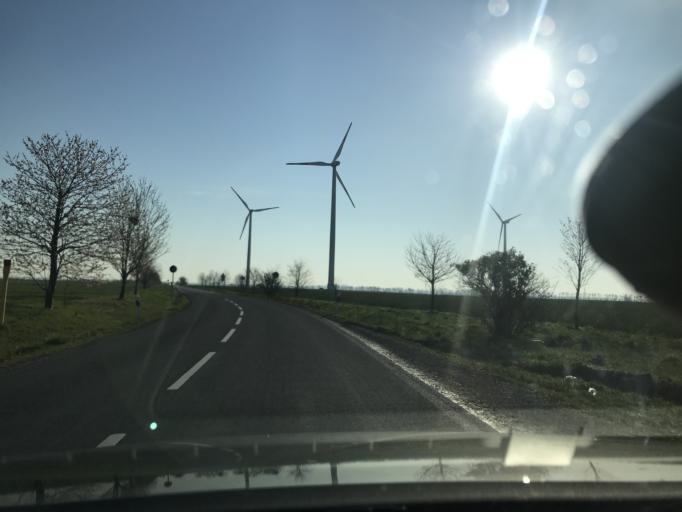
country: DE
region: Saxony-Anhalt
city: Holleben
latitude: 51.4266
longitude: 11.8692
